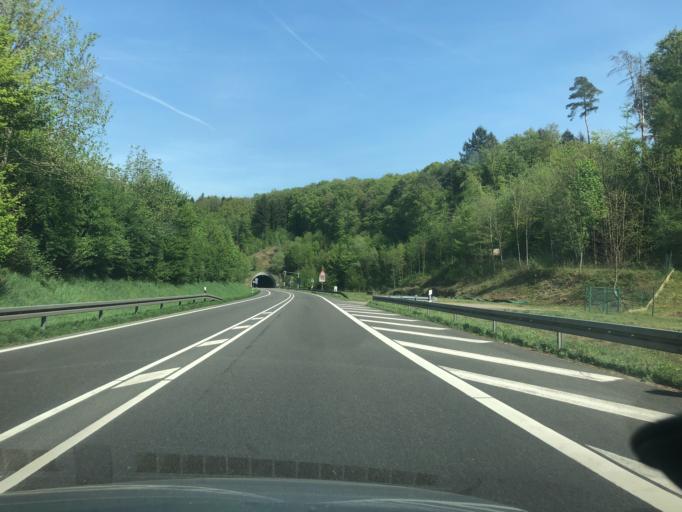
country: CH
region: Aargau
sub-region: Bezirk Zurzach
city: Koblenz
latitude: 47.6234
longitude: 8.2672
